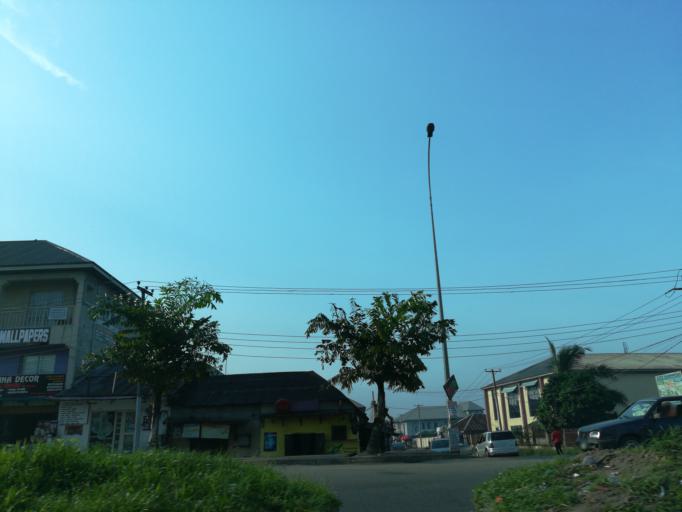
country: NG
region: Rivers
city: Port Harcourt
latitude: 4.8221
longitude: 7.0192
